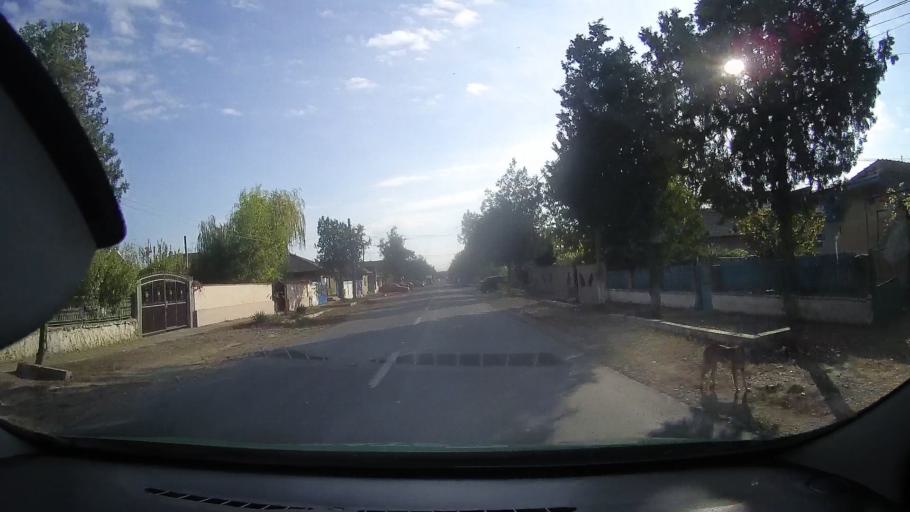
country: RO
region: Constanta
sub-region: Comuna Corbu
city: Corbu
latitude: 44.3843
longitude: 28.6623
